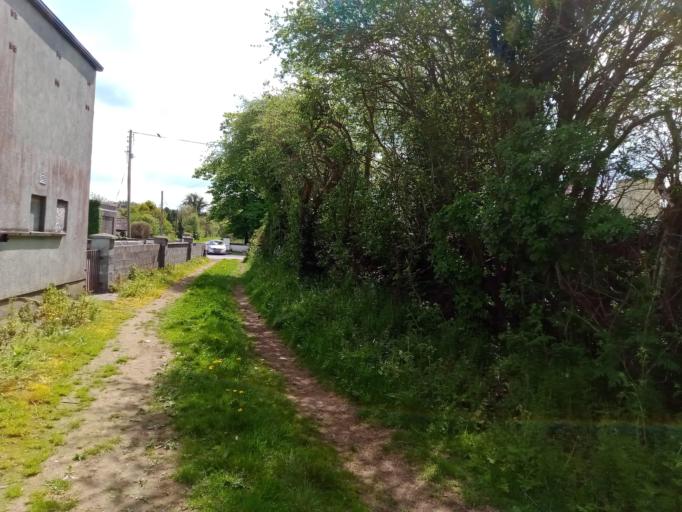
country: IE
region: Leinster
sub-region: Kilkenny
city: Ballyragget
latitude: 52.7319
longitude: -7.4076
